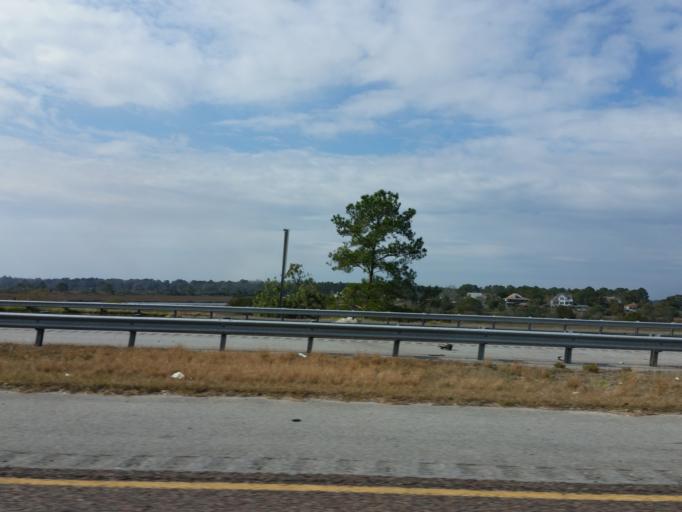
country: US
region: Georgia
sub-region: Liberty County
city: Midway
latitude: 31.8306
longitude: -81.3543
